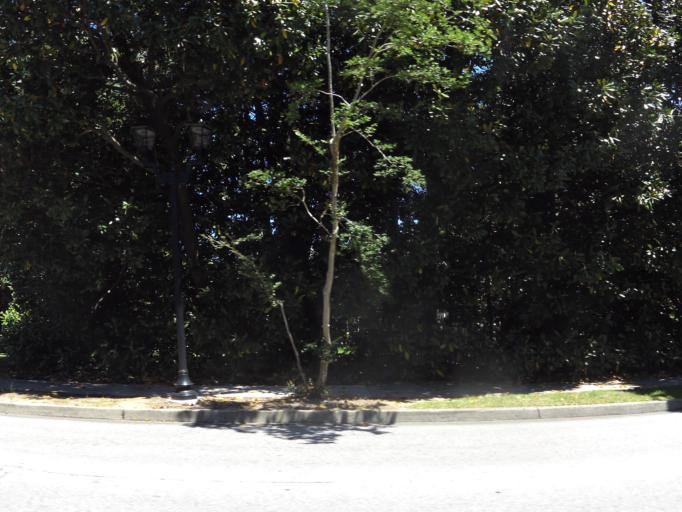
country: US
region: Georgia
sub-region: Richmond County
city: Augusta
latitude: 33.4779
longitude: -82.0184
